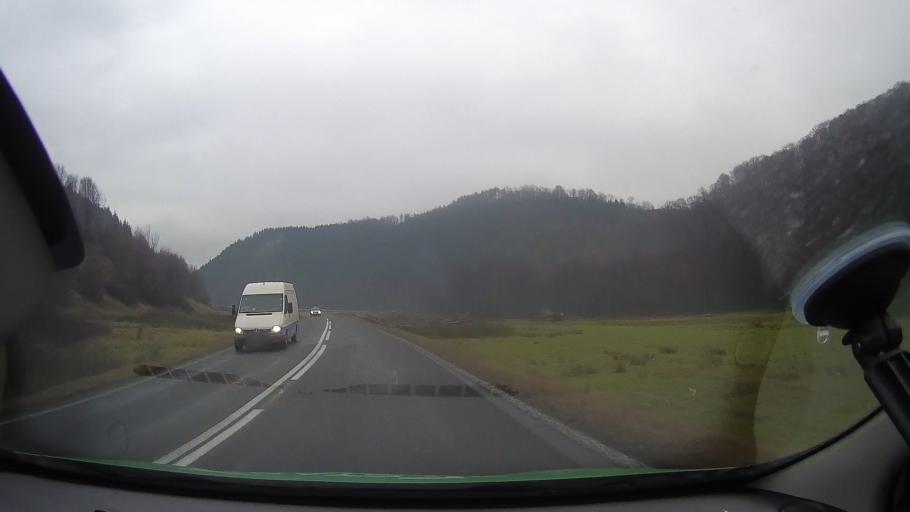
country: RO
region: Arad
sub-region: Comuna Plescuta
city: Plescuta
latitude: 46.3157
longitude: 22.4691
